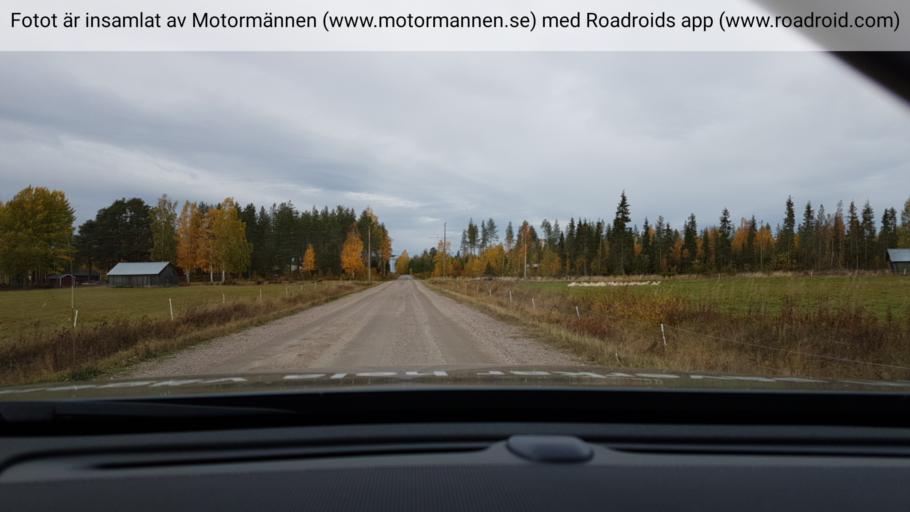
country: SE
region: Norrbotten
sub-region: Overkalix Kommun
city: OEverkalix
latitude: 66.3030
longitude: 22.9278
